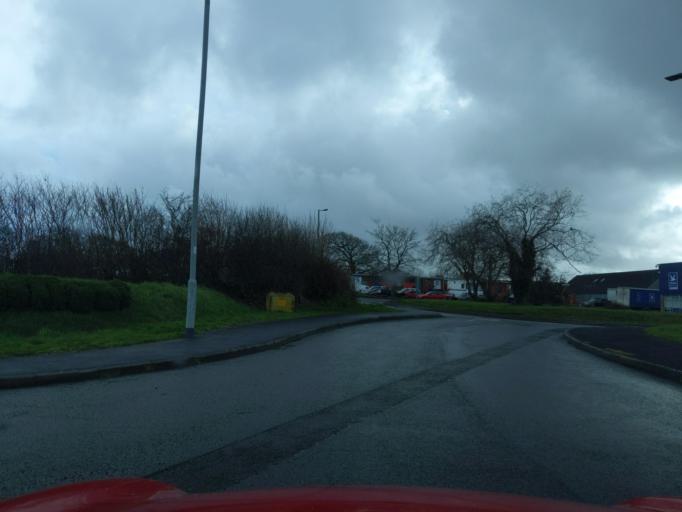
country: GB
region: England
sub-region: Devon
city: Great Torrington
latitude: 50.9563
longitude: -4.1245
